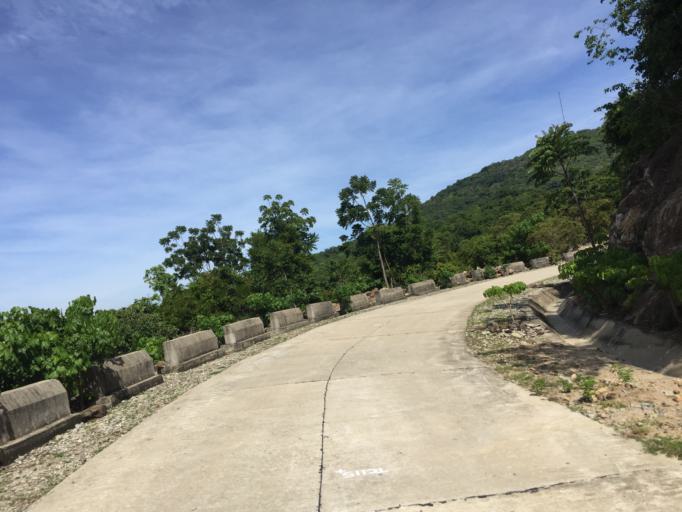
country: VN
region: Quang Nam
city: Hoi An
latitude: 15.9327
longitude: 108.5309
